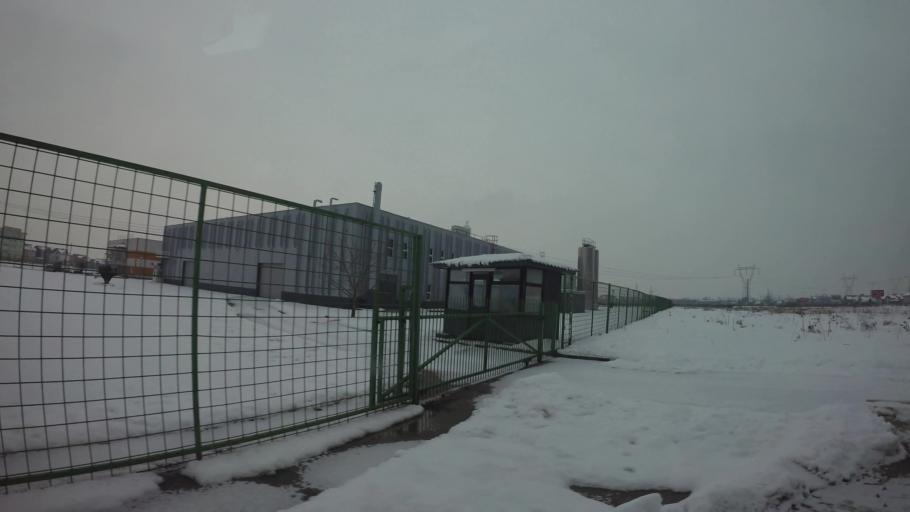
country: BA
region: Federation of Bosnia and Herzegovina
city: Hadzici
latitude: 43.8355
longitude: 18.2689
